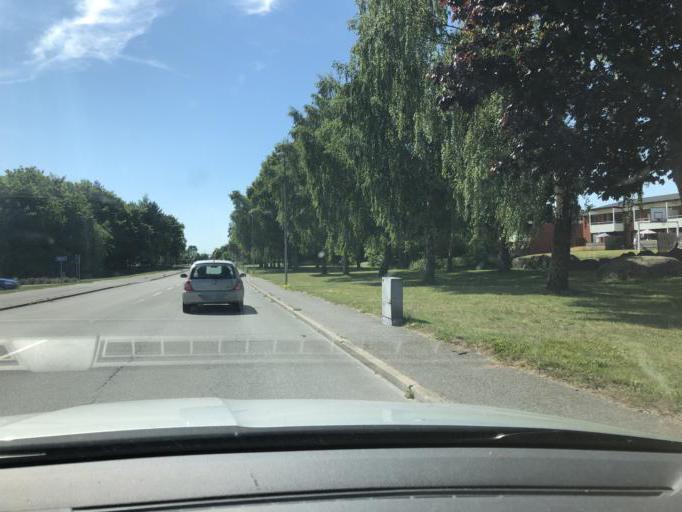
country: SE
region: Skane
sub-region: Bromolla Kommun
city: Bromoella
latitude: 56.0761
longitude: 14.4896
